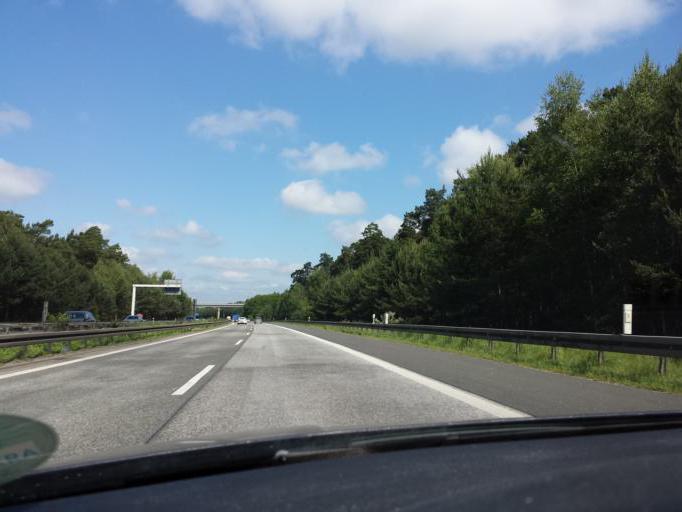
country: DE
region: Brandenburg
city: Hohen Neuendorf
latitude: 52.6632
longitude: 13.2421
